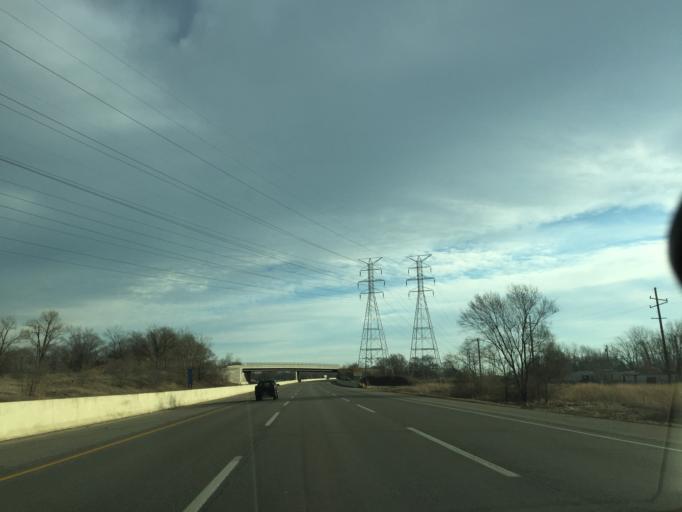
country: US
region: Indiana
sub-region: Lake County
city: New Chicago
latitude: 41.5865
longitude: -87.2888
